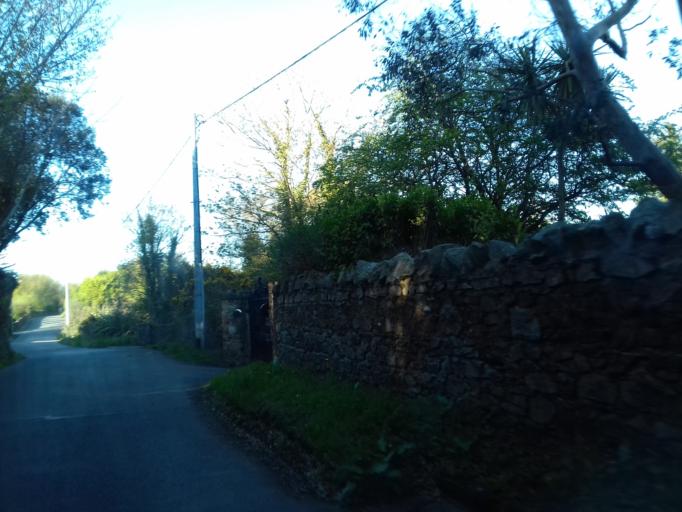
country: IE
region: Leinster
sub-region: Fingal County
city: Howth
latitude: 53.3714
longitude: -6.0637
